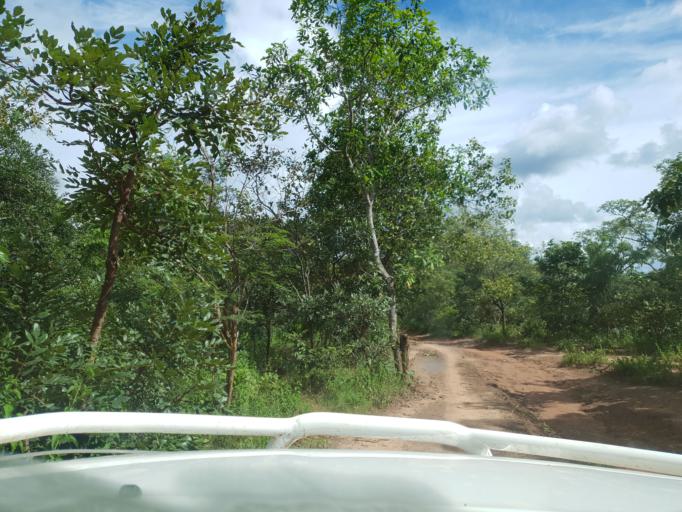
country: CI
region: Savanes
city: Tengrela
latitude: 10.4615
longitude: -6.7966
